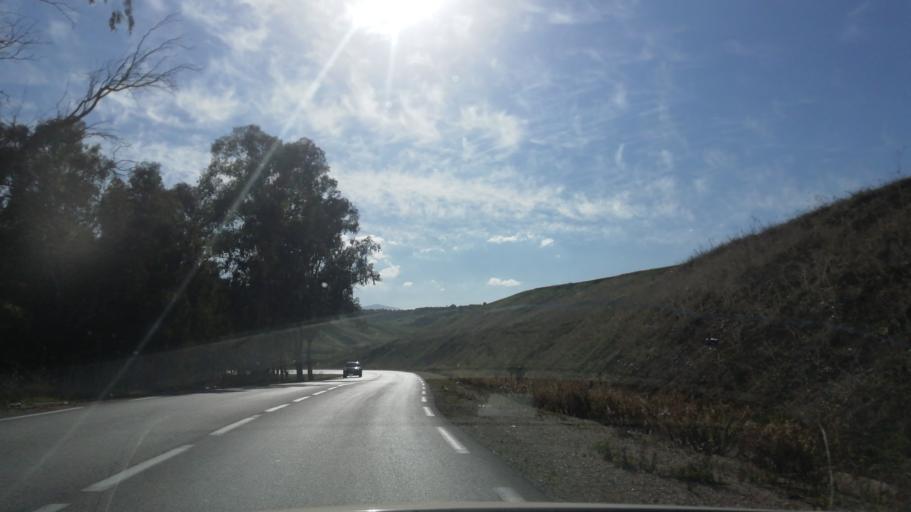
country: DZ
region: Tlemcen
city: Chetouane
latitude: 34.9758
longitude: -1.2391
